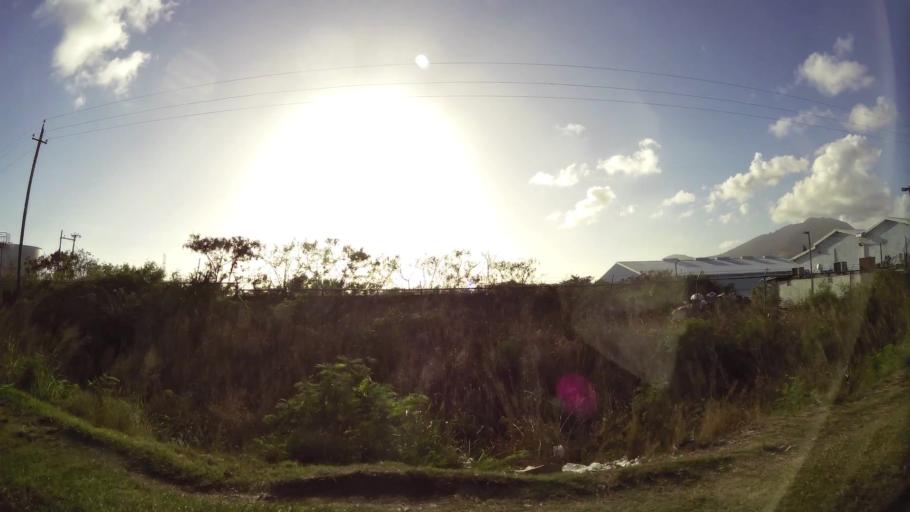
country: KN
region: Saint George Basseterre
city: Basseterre
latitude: 17.2945
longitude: -62.7083
